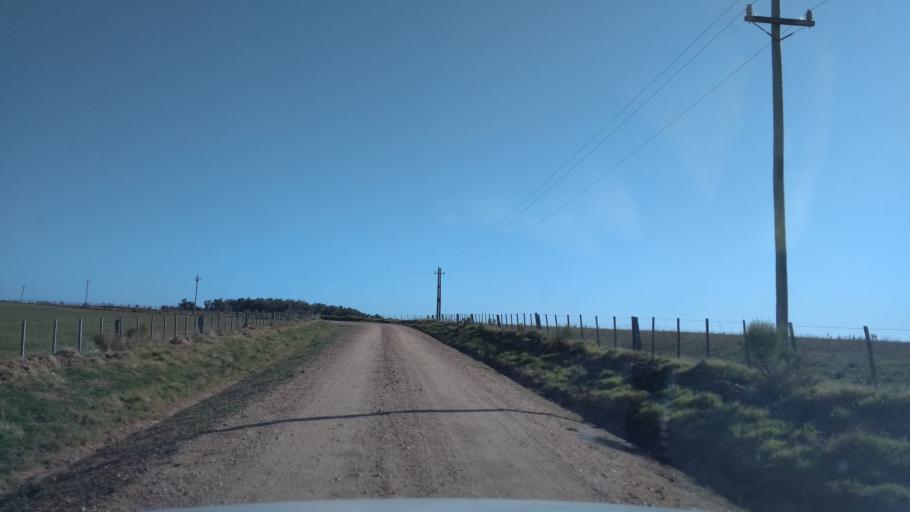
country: UY
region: Florida
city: Casupa
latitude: -34.0359
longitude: -55.7803
